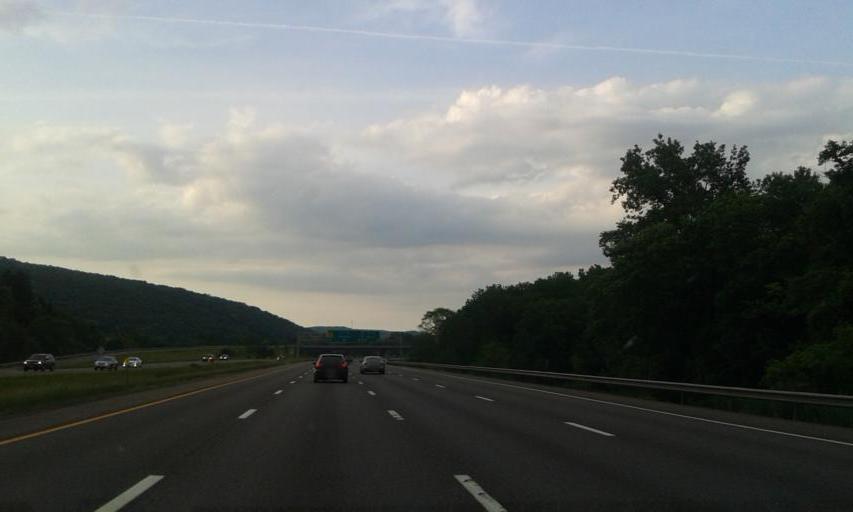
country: US
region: New York
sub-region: Broome County
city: Port Dickinson
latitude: 42.1370
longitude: -75.9024
